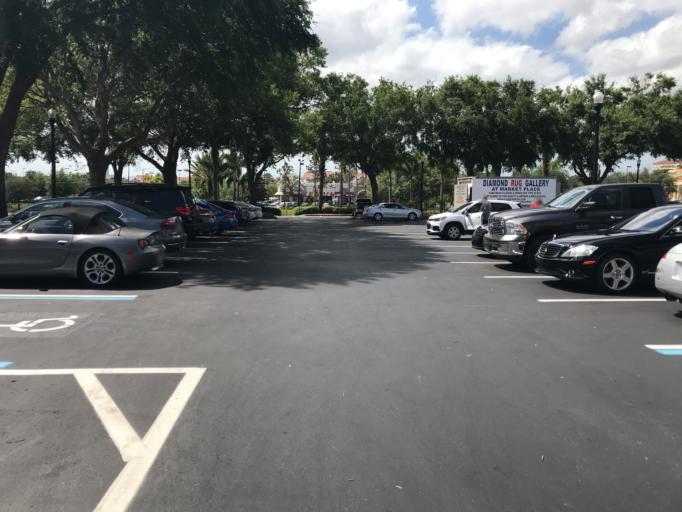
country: US
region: Florida
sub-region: Orange County
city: Doctor Phillips
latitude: 28.4509
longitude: -81.4901
